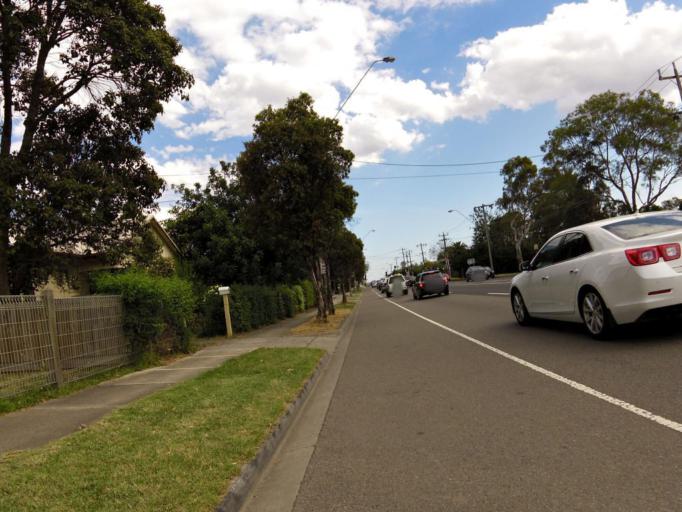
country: AU
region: Victoria
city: Watsonia
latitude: -37.7176
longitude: 145.0816
